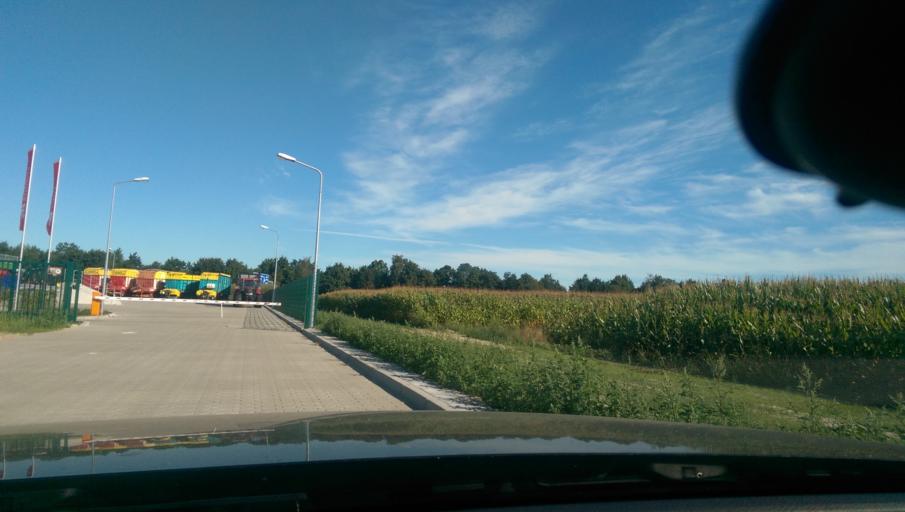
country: DE
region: Lower Saxony
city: Oyten
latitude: 53.0515
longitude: 9.0412
